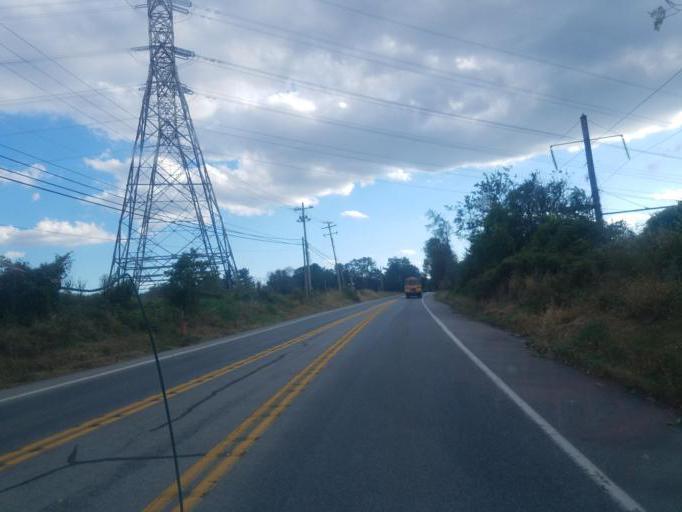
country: US
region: Pennsylvania
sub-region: Dauphin County
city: Middletown
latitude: 40.1621
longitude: -76.7176
